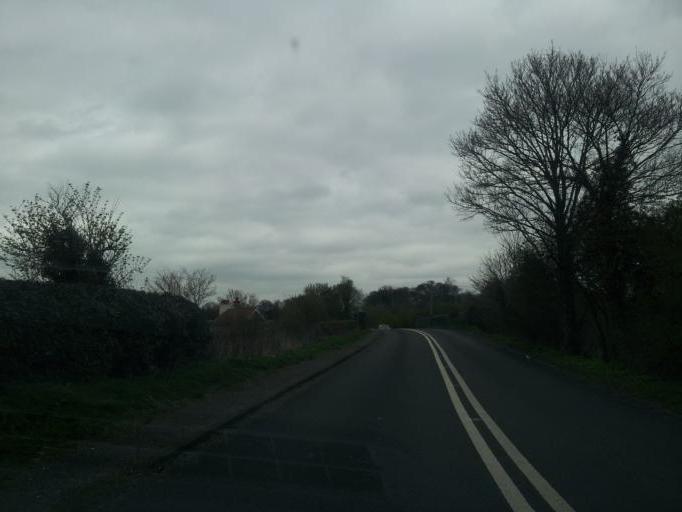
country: GB
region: England
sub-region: Hertfordshire
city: Great Munden
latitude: 51.8979
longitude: 0.0186
